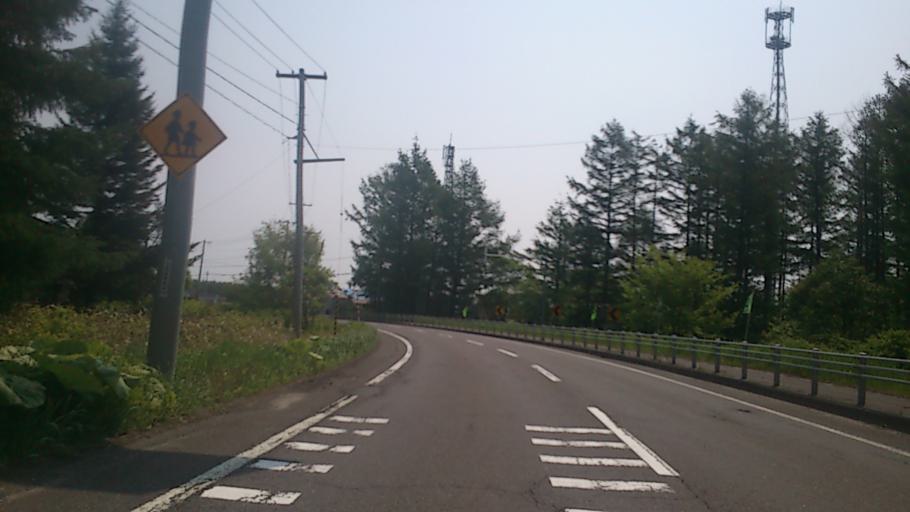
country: JP
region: Hokkaido
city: Shibetsu
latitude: 43.3654
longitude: 144.9845
